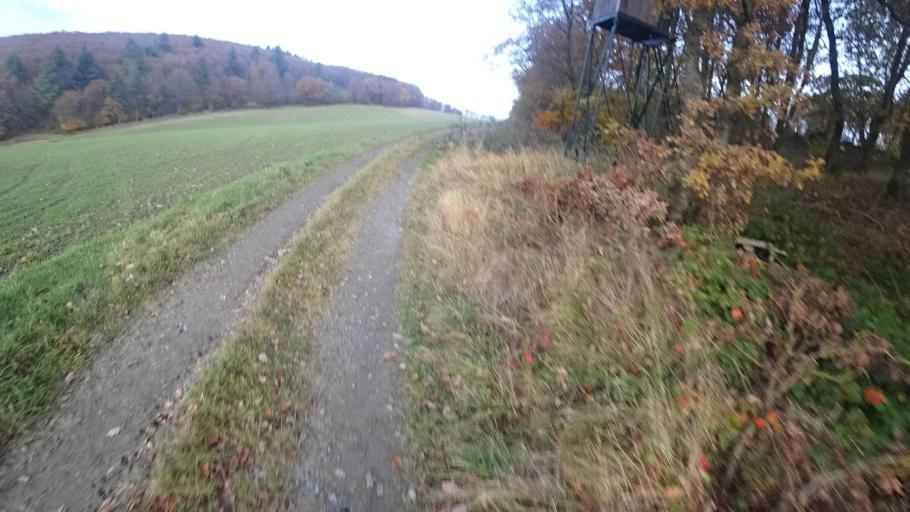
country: DE
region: Rheinland-Pfalz
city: Utzenhain
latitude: 50.1317
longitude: 7.6466
